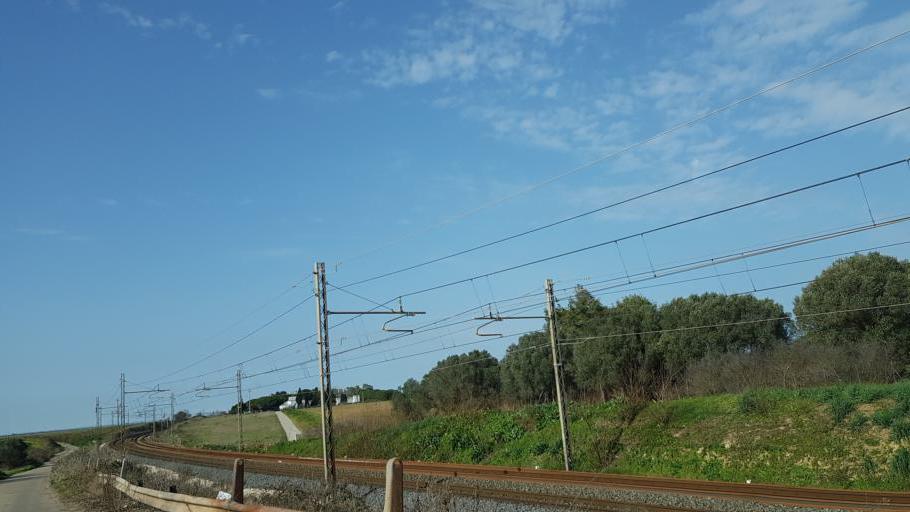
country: IT
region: Apulia
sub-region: Provincia di Brindisi
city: Brindisi
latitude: 40.6232
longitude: 17.9035
